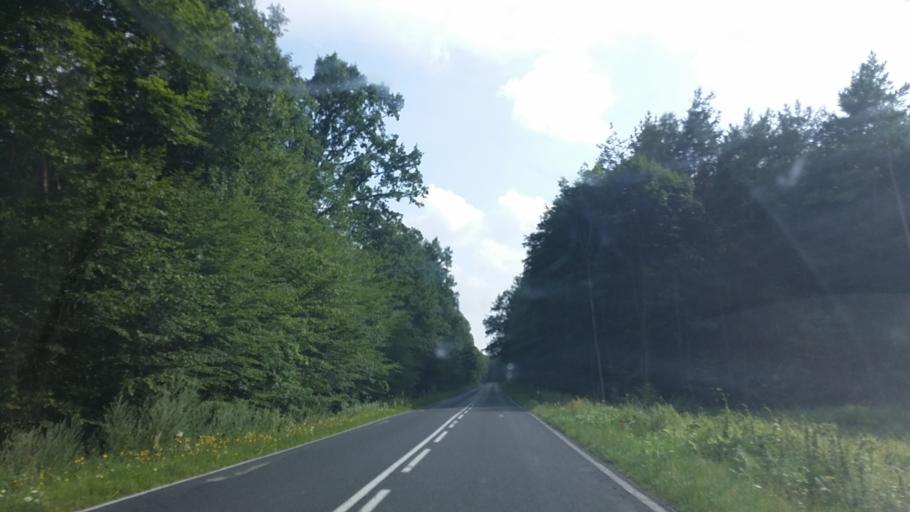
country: PL
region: West Pomeranian Voivodeship
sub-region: Powiat mysliborski
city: Barlinek
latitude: 52.9098
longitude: 15.1939
